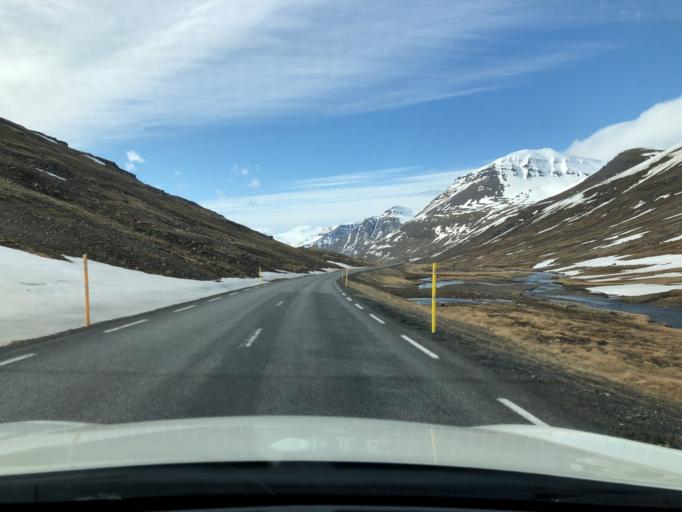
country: IS
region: East
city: Reydarfjoerdur
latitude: 65.0907
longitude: -14.3298
